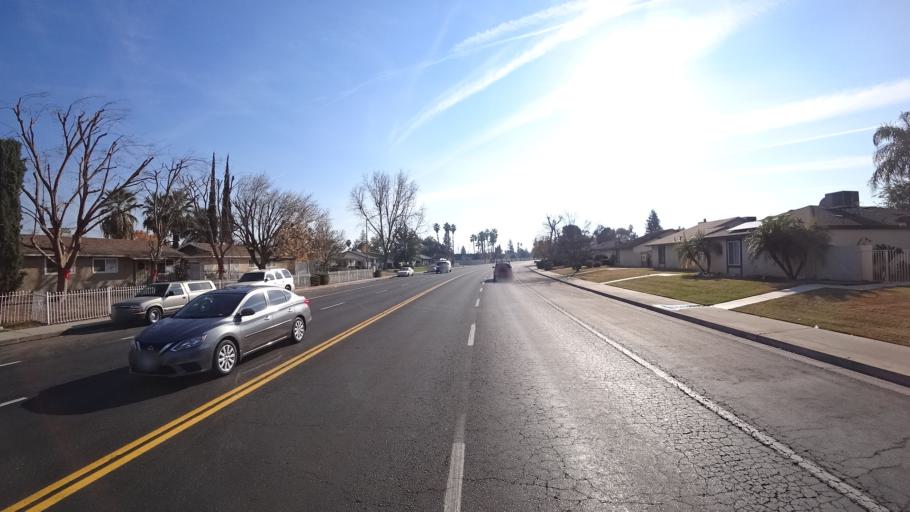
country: US
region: California
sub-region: Kern County
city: Bakersfield
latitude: 35.3245
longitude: -119.0658
